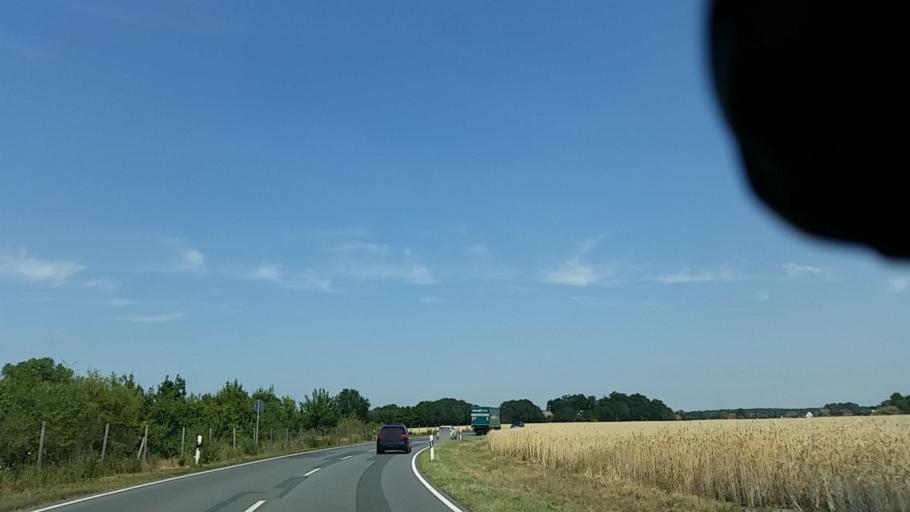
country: DE
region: Lower Saxony
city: Syke
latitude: 52.9488
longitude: 8.8263
